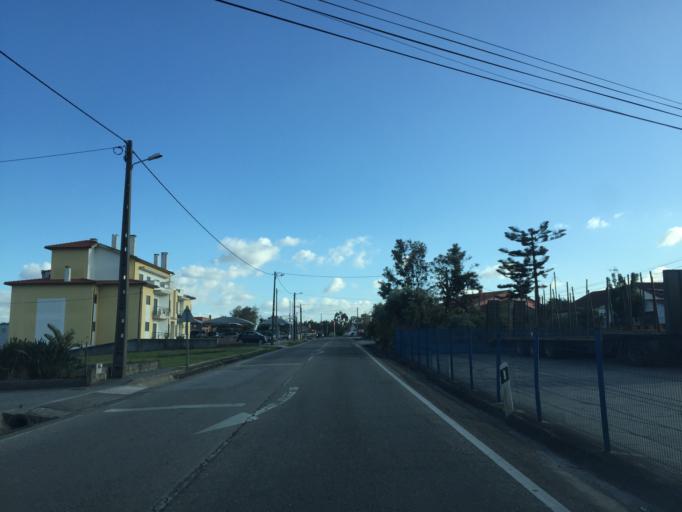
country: PT
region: Leiria
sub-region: Pombal
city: Lourical
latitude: 39.9666
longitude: -8.7917
